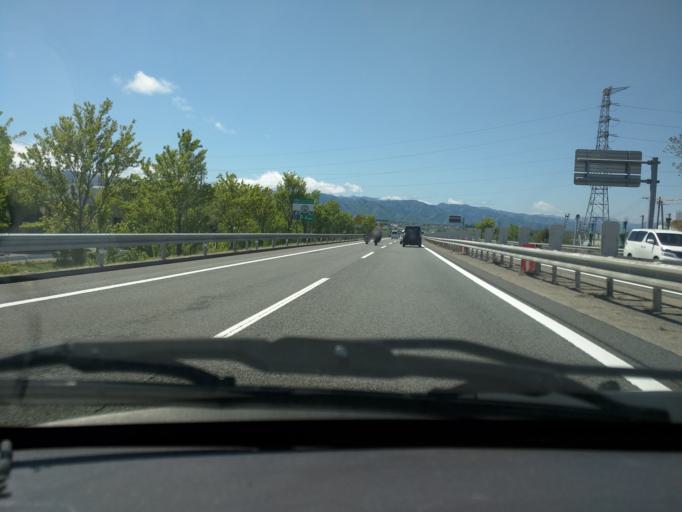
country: JP
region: Nagano
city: Nakano
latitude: 36.7271
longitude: 138.3166
